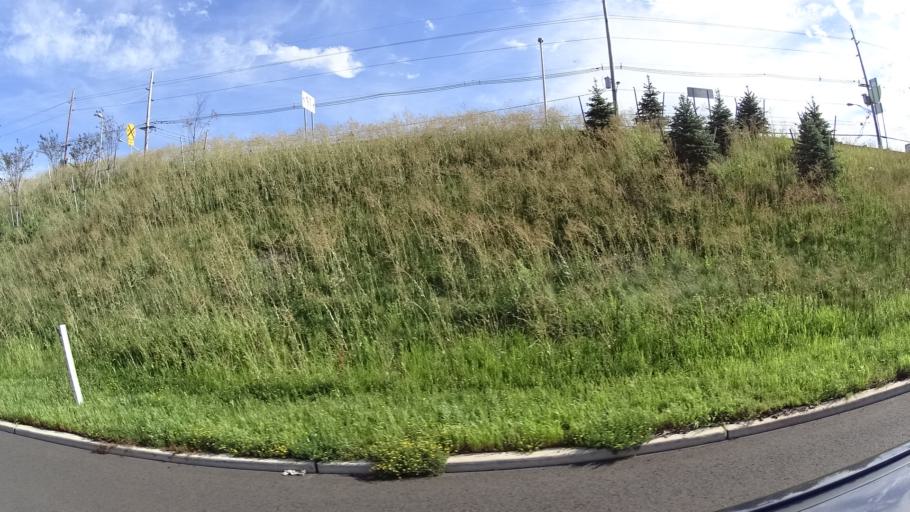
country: US
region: New Jersey
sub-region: Somerset County
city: Finderne
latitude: 40.5752
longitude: -74.5624
